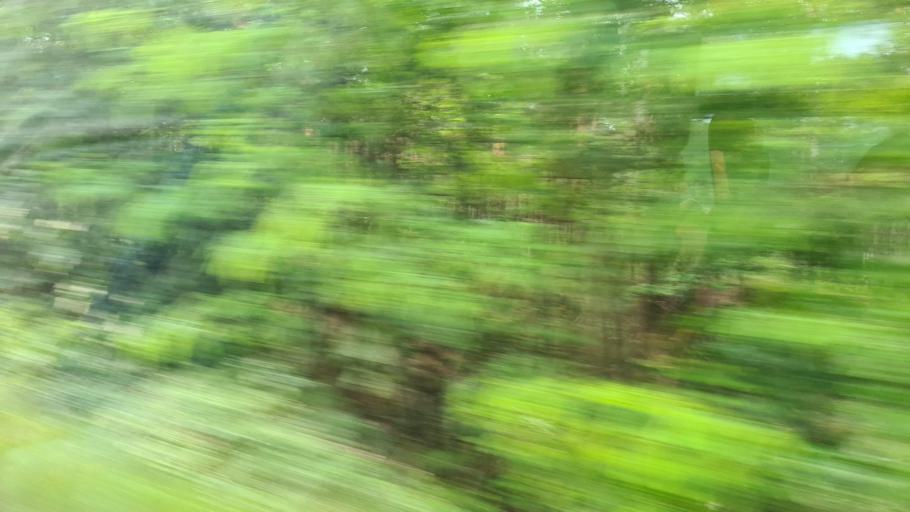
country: DE
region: Brandenburg
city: Finsterwalde
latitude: 51.6282
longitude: 13.6613
